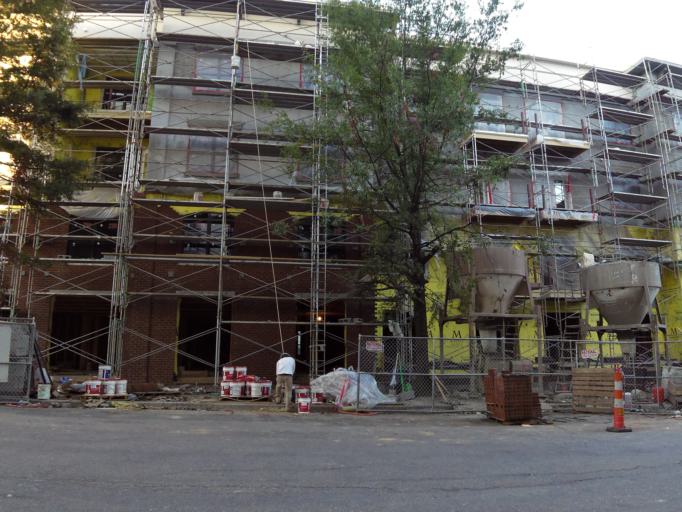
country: US
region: Tennessee
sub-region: Knox County
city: Knoxville
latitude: 35.9674
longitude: -83.9183
